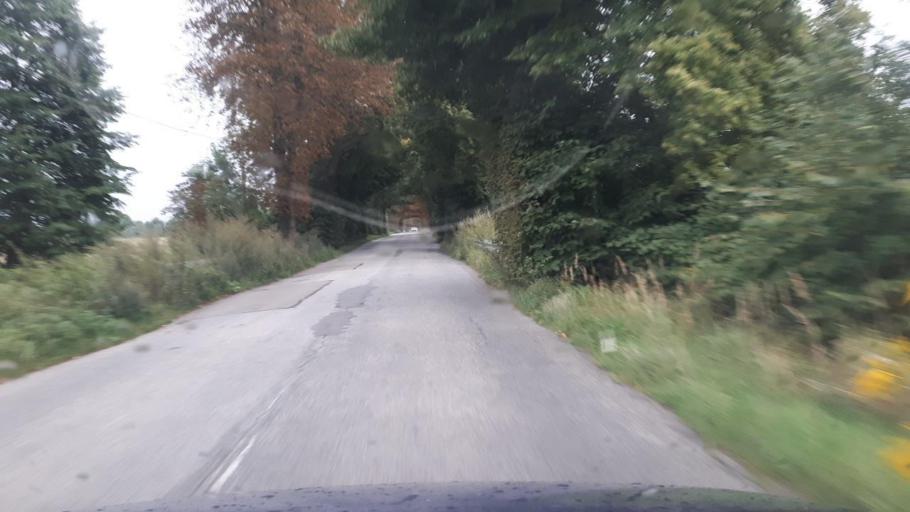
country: PL
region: Silesian Voivodeship
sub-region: Powiat tarnogorski
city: Wieszowa
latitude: 50.3741
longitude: 18.7166
